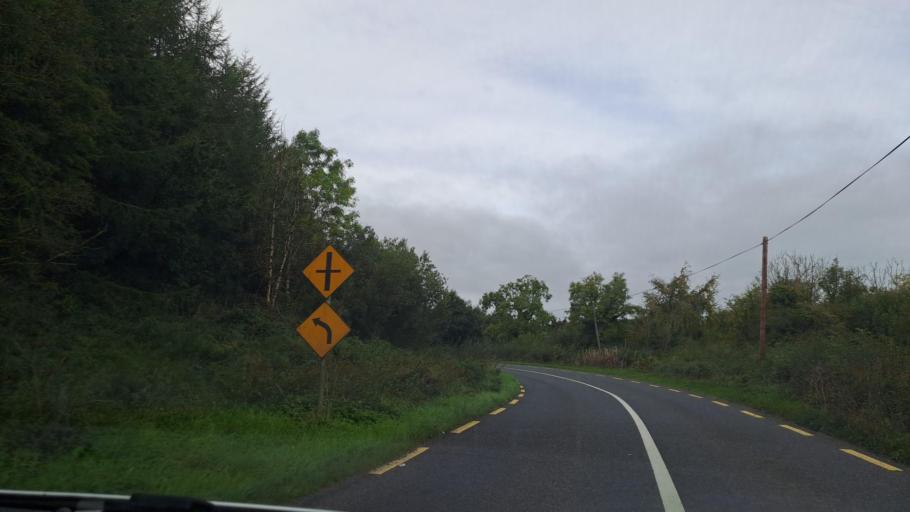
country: IE
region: Ulster
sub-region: County Monaghan
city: Carrickmacross
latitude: 53.8725
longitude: -6.7046
